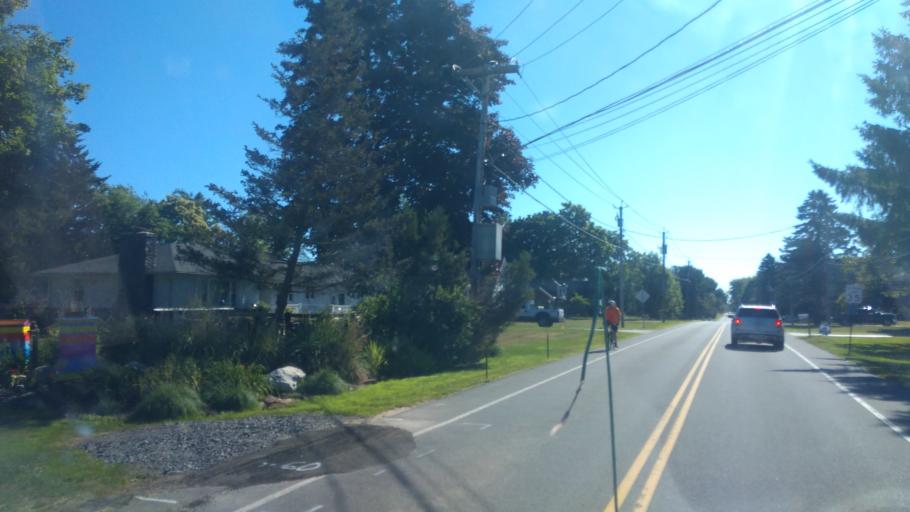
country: US
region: New York
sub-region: Monroe County
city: Webster
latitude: 43.2370
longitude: -77.4676
